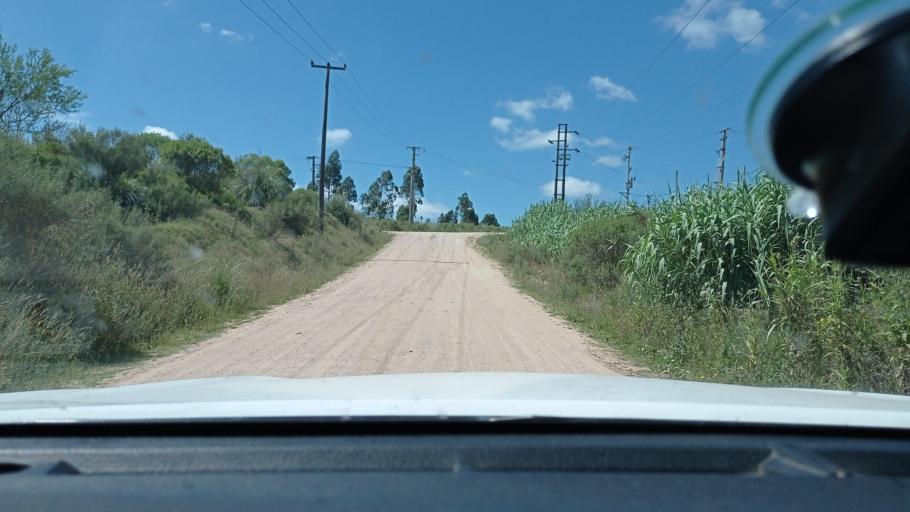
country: UY
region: Canelones
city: Pando
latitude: -34.7256
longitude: -55.9736
